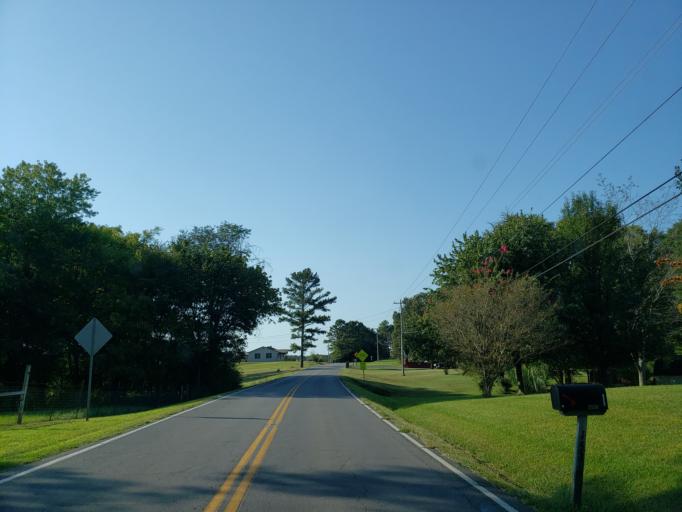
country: US
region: Tennessee
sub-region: Bradley County
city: Wildwood Lake
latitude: 35.0835
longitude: -84.7910
